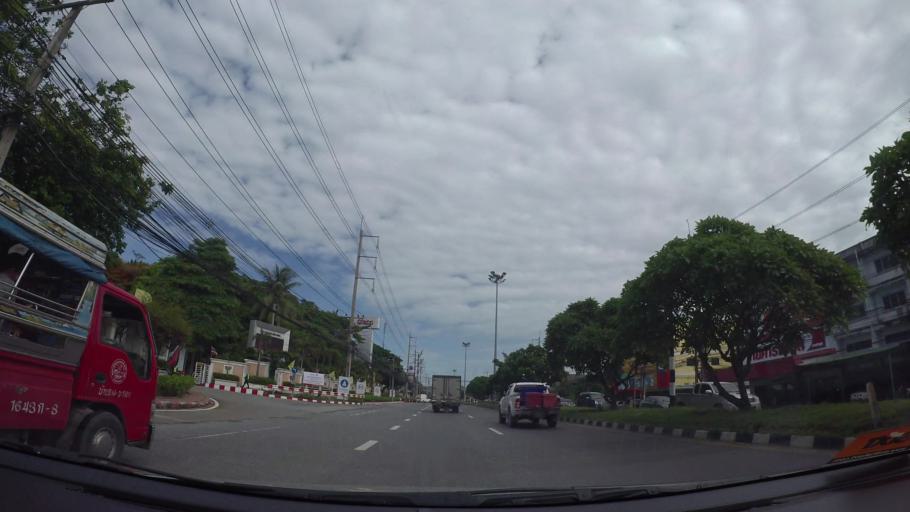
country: TH
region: Rayong
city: Ban Chang
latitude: 12.7219
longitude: 101.1537
